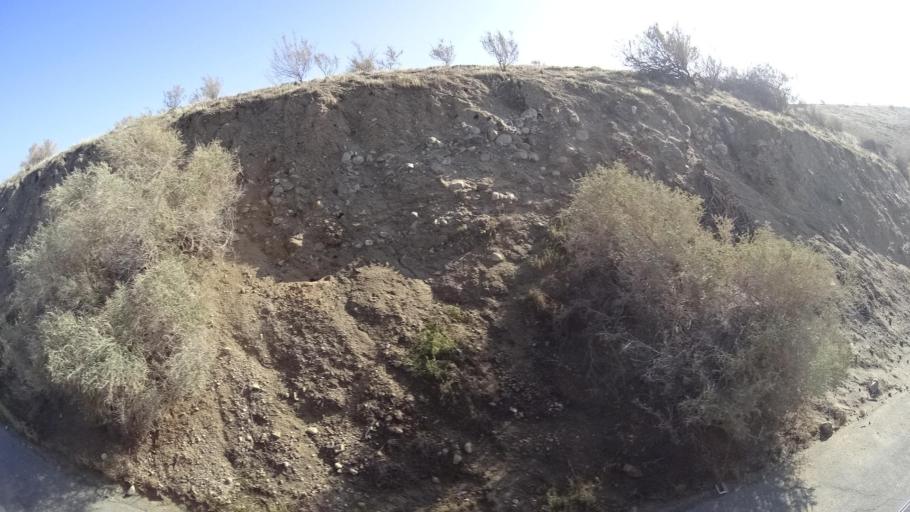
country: US
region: California
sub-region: Kern County
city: Taft Heights
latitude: 35.1285
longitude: -119.4709
